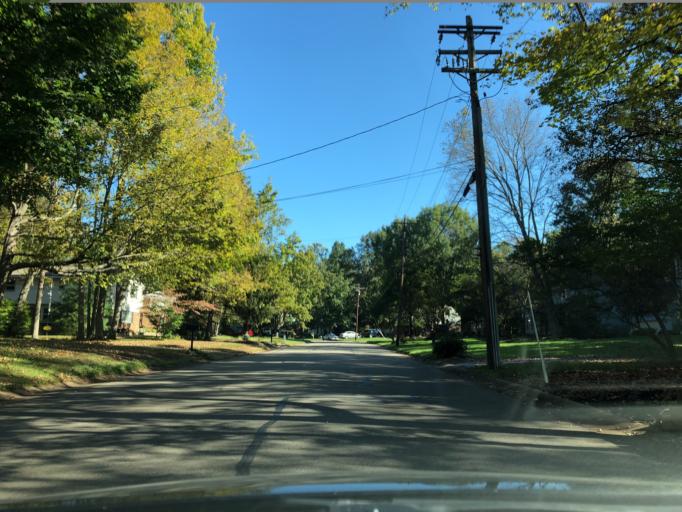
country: US
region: Ohio
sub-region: Hamilton County
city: The Village of Indian Hill
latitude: 39.2599
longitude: -84.2942
